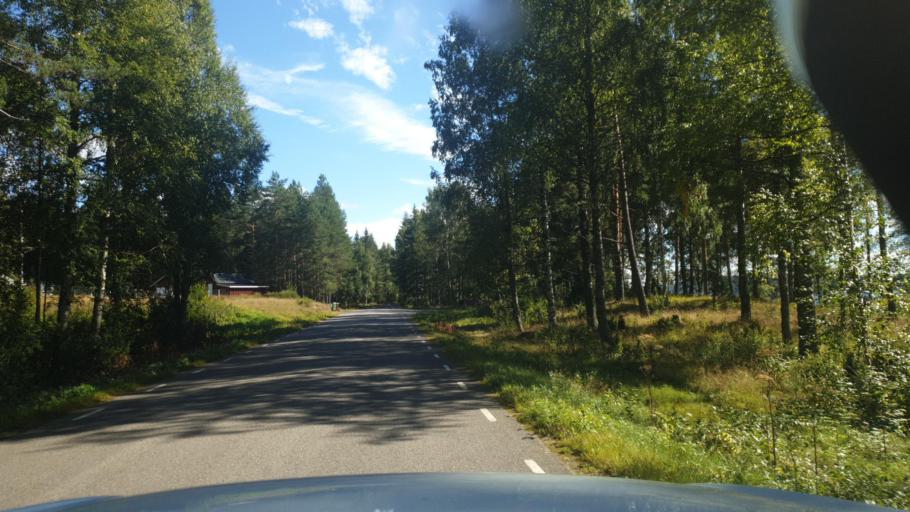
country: SE
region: Vaermland
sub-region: Torsby Kommun
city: Torsby
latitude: 60.0056
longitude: 12.7159
